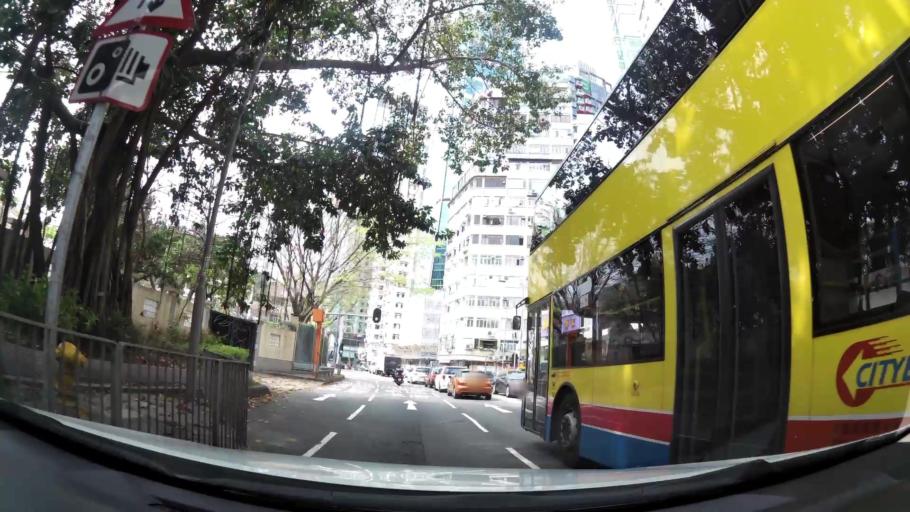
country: HK
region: Wanchai
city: Wan Chai
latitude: 22.2848
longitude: 114.1903
